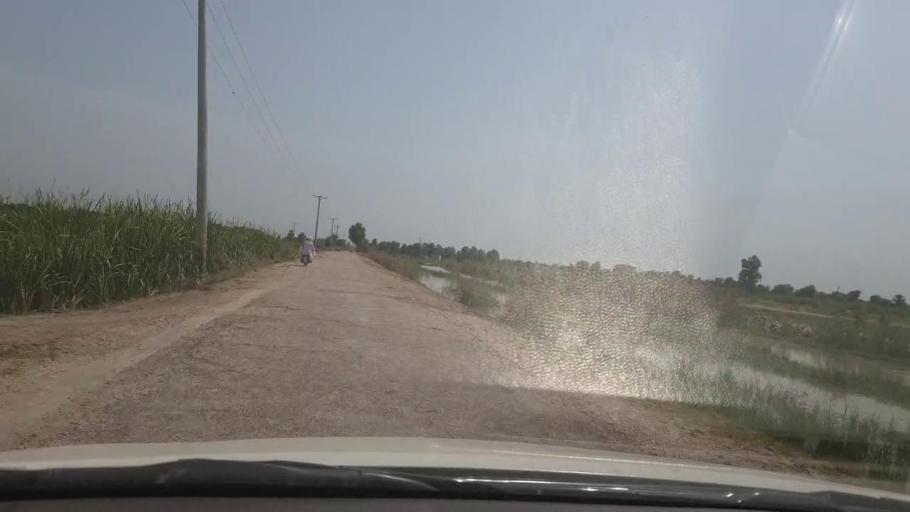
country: PK
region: Sindh
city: Garhi Yasin
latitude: 27.9798
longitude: 68.5027
